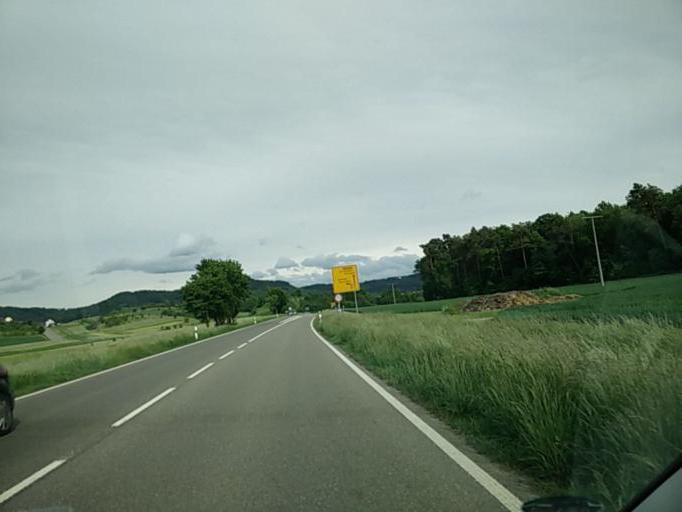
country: DE
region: Baden-Wuerttemberg
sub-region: Regierungsbezirk Stuttgart
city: Hildrizhausen
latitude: 48.5681
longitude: 8.9421
